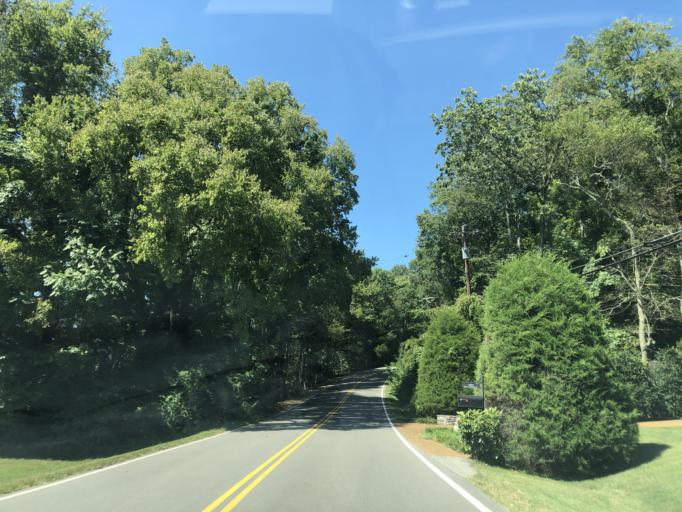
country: US
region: Tennessee
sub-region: Davidson County
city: Forest Hills
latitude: 36.0652
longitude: -86.8358
